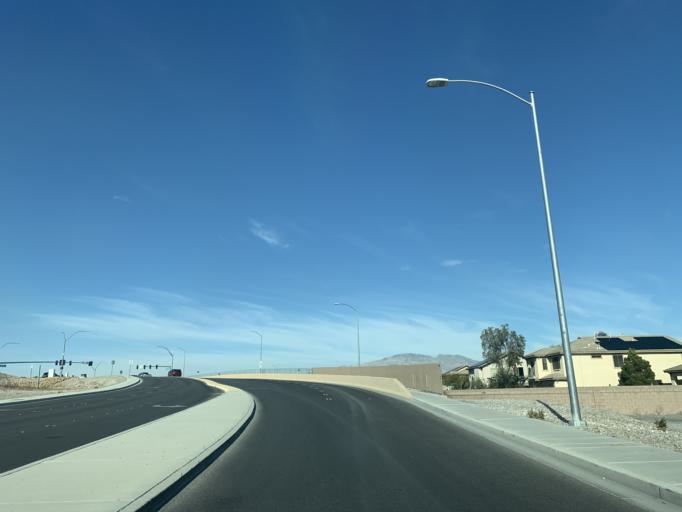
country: US
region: Nevada
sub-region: Clark County
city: Summerlin South
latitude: 36.3140
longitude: -115.2967
